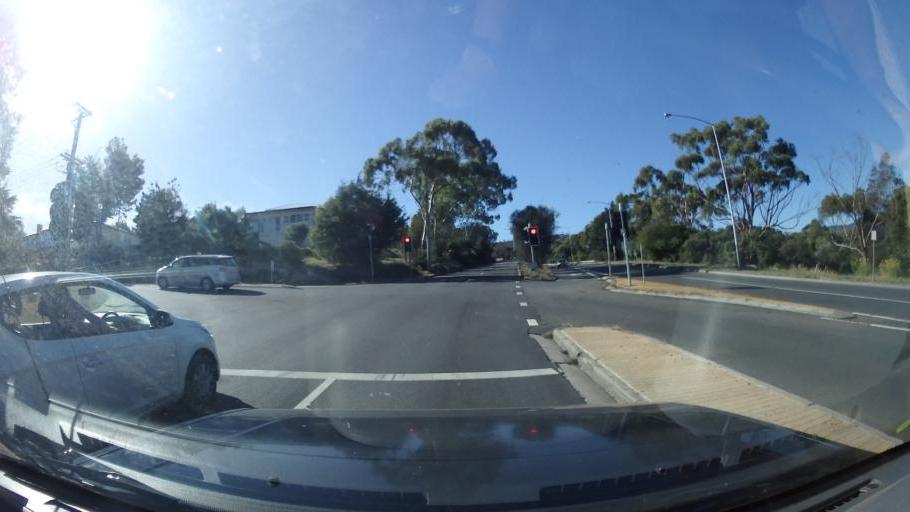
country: AU
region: Tasmania
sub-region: Clarence
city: Bellerive
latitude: -42.8661
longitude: 147.3650
